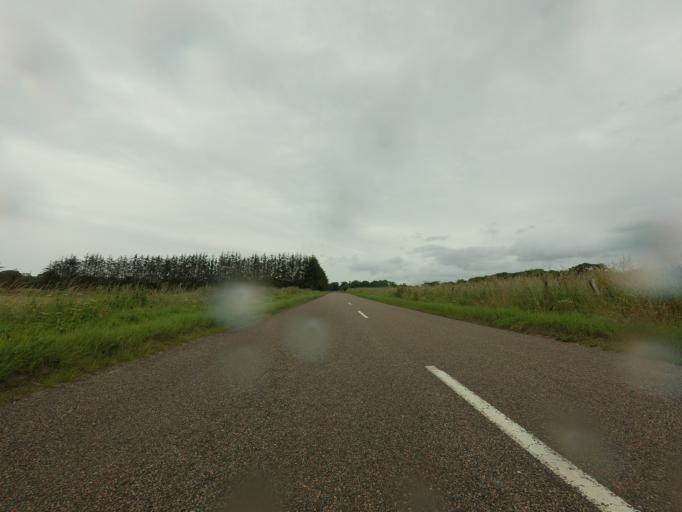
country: GB
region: Scotland
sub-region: Moray
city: Cullen
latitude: 57.6792
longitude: -2.8133
